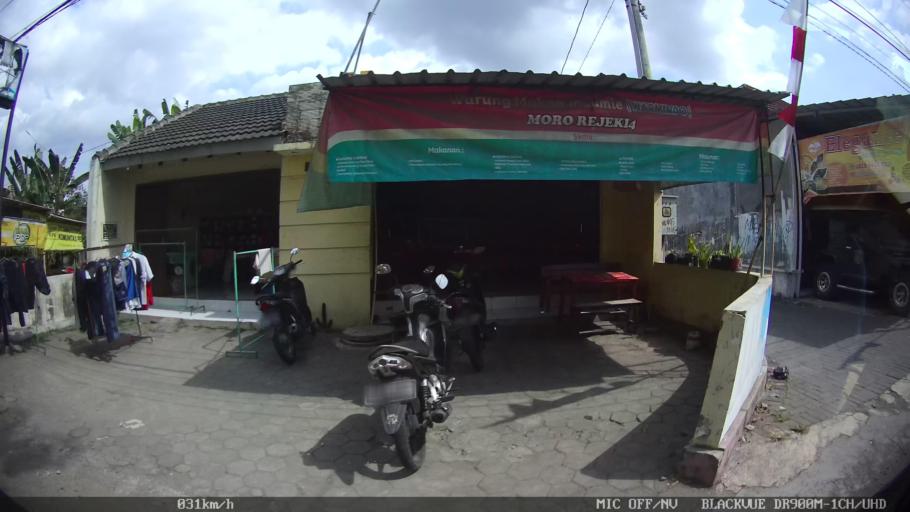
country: ID
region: Daerah Istimewa Yogyakarta
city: Gamping Lor
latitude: -7.8057
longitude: 110.3346
